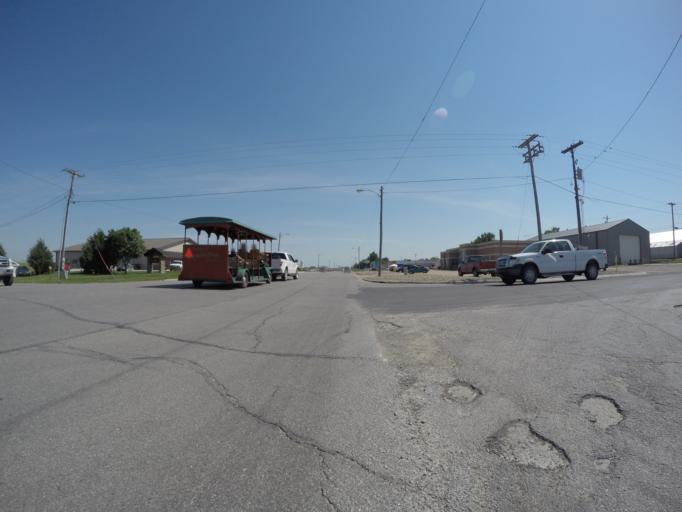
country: US
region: Kansas
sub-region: Nemaha County
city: Sabetha
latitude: 39.8998
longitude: -95.7883
